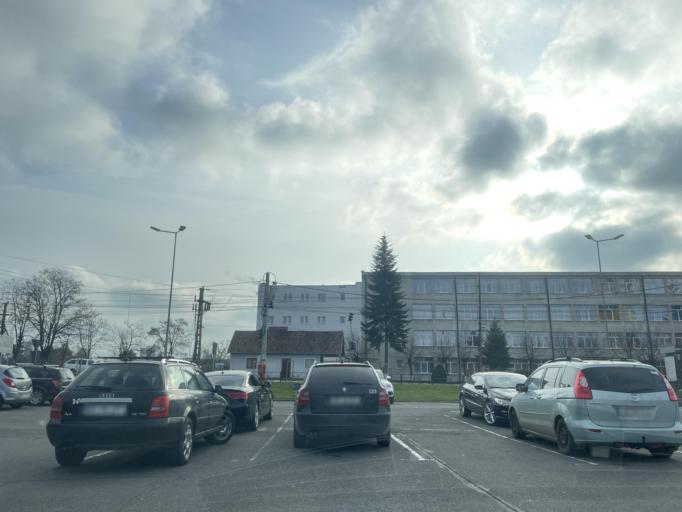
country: RO
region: Mures
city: Reghin-Sat
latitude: 46.7786
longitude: 24.7124
